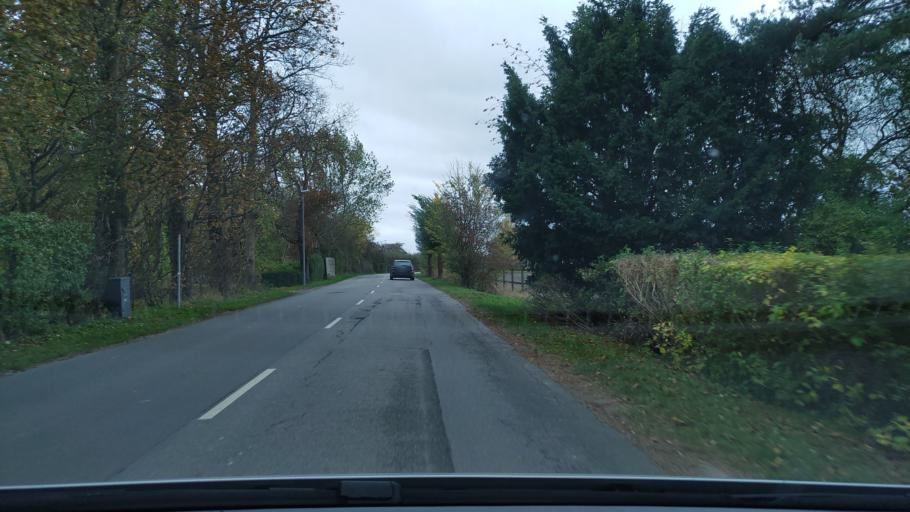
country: DK
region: Capital Region
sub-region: Tarnby Kommune
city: Tarnby
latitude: 55.5997
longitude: 12.6032
